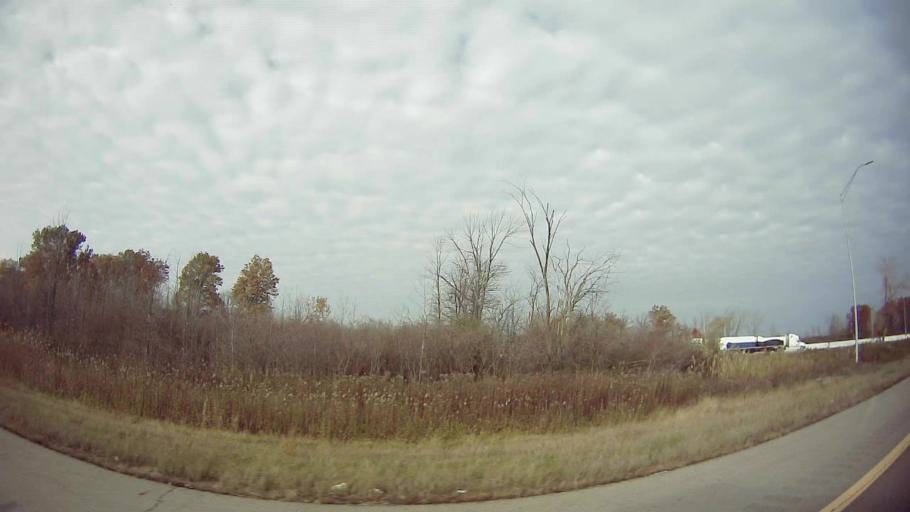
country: US
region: Michigan
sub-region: Monroe County
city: Woodland Beach
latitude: 41.9871
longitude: -83.3292
